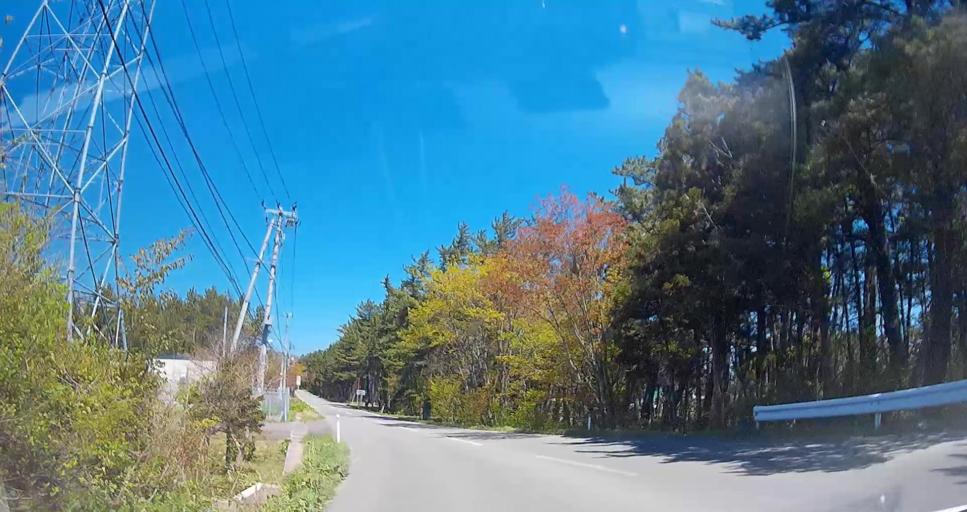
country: JP
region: Aomori
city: Mutsu
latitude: 41.0633
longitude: 141.3867
